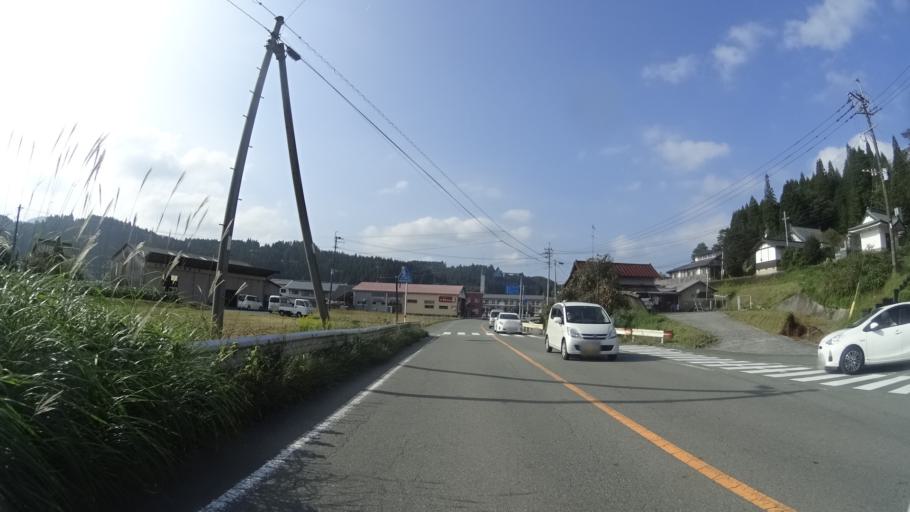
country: JP
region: Kumamoto
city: Aso
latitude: 33.1078
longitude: 131.0649
